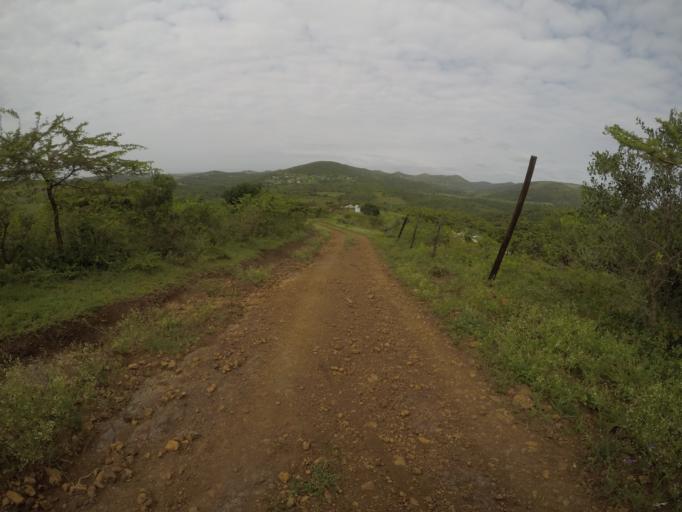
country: ZA
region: KwaZulu-Natal
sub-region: uThungulu District Municipality
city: Empangeni
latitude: -28.6269
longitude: 31.9012
